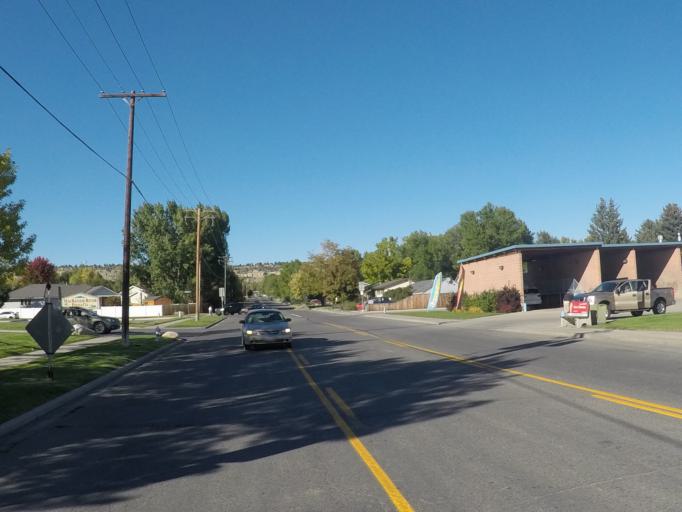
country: US
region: Montana
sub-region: Yellowstone County
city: Billings
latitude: 45.7849
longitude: -108.5903
